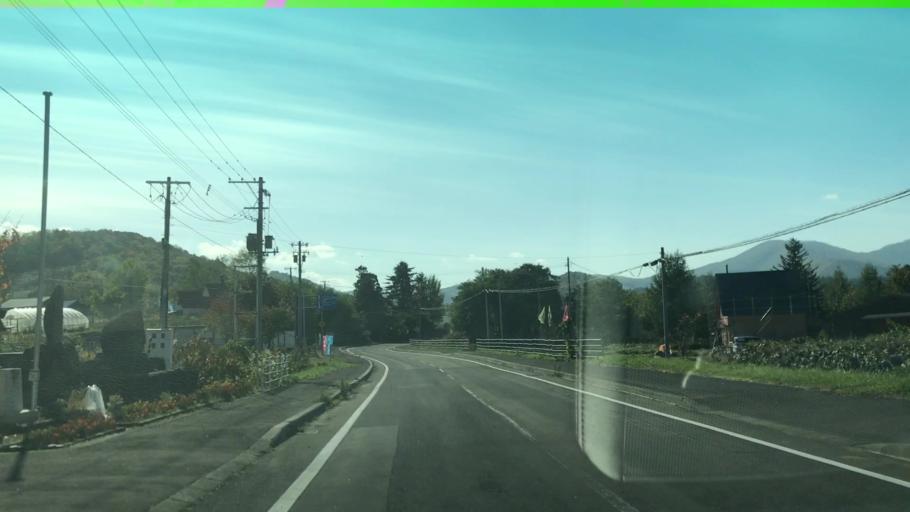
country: JP
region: Hokkaido
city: Yoichi
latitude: 43.1664
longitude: 140.8216
